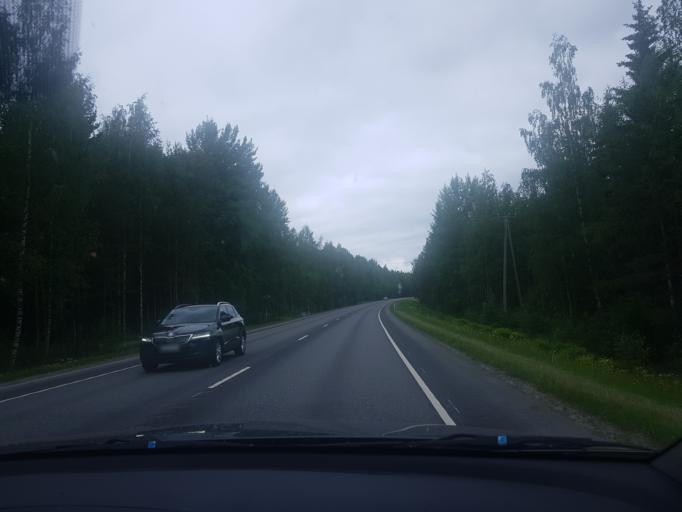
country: FI
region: Pirkanmaa
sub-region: Tampere
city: Kangasala
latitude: 61.4046
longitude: 24.1742
